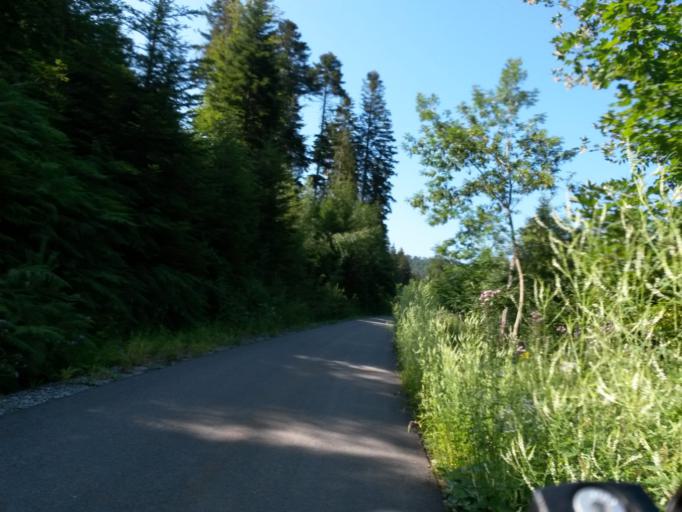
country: DE
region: Baden-Wuerttemberg
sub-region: Karlsruhe Region
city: Bad Wildbad
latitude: 48.7094
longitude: 8.5442
